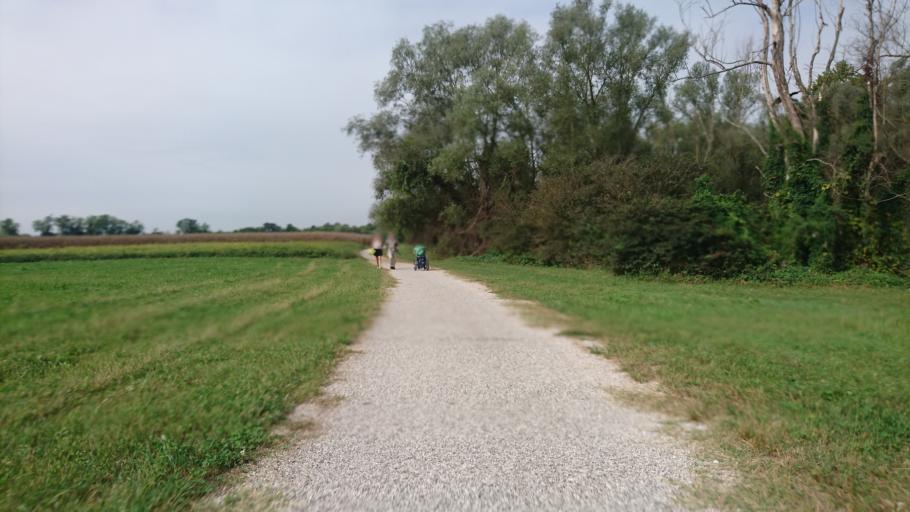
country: IT
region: Veneto
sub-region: Provincia di Padova
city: Piazzola sul Brenta
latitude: 45.5653
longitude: 11.7821
